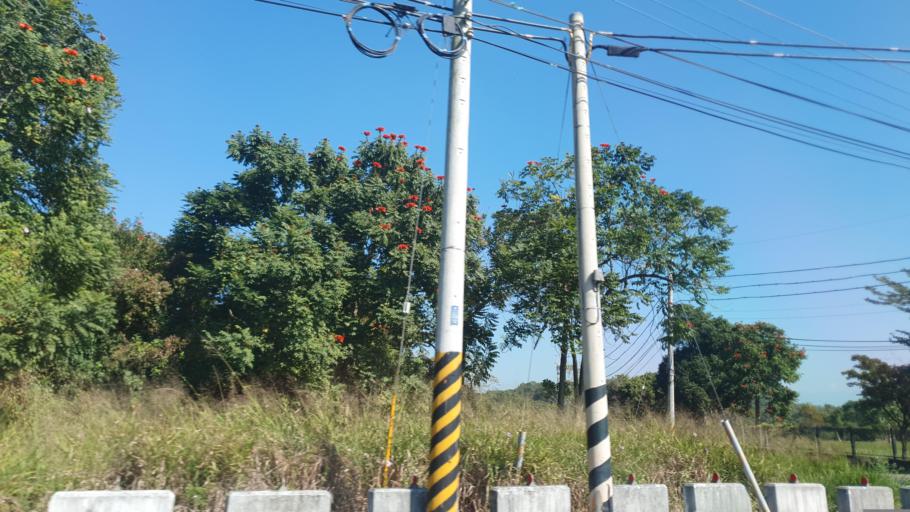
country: TW
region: Taiwan
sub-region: Tainan
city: Tainan
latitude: 23.0340
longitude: 120.3476
